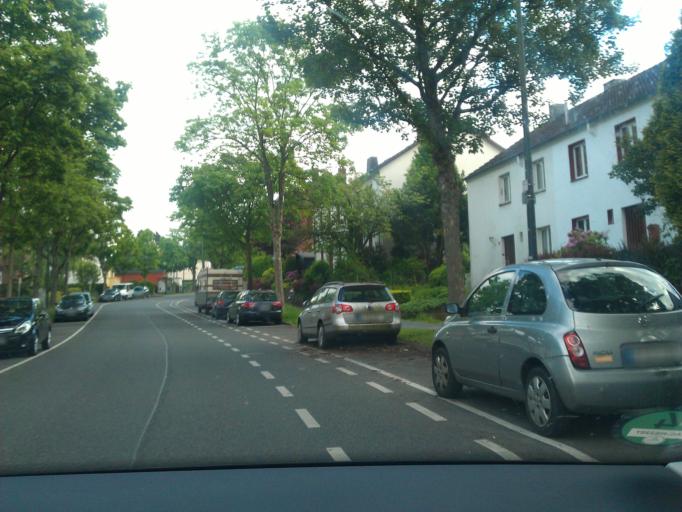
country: DE
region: North Rhine-Westphalia
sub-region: Regierungsbezirk Koln
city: Aachen
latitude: 50.7641
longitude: 6.1100
